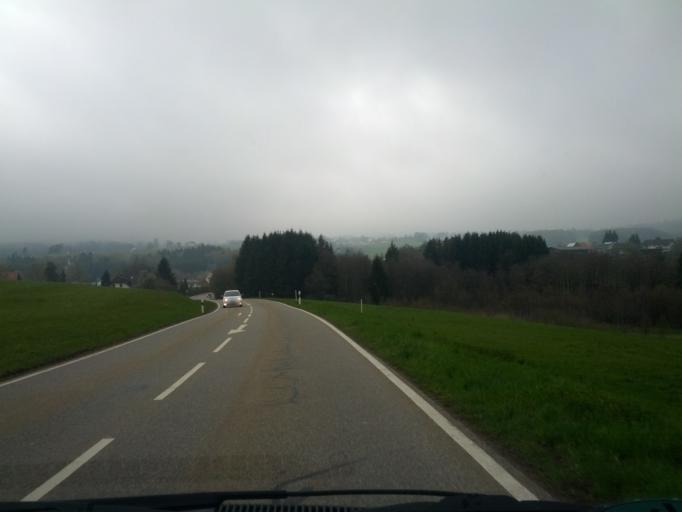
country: DE
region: Baden-Wuerttemberg
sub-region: Freiburg Region
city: Rickenbach
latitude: 47.6204
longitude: 8.0150
